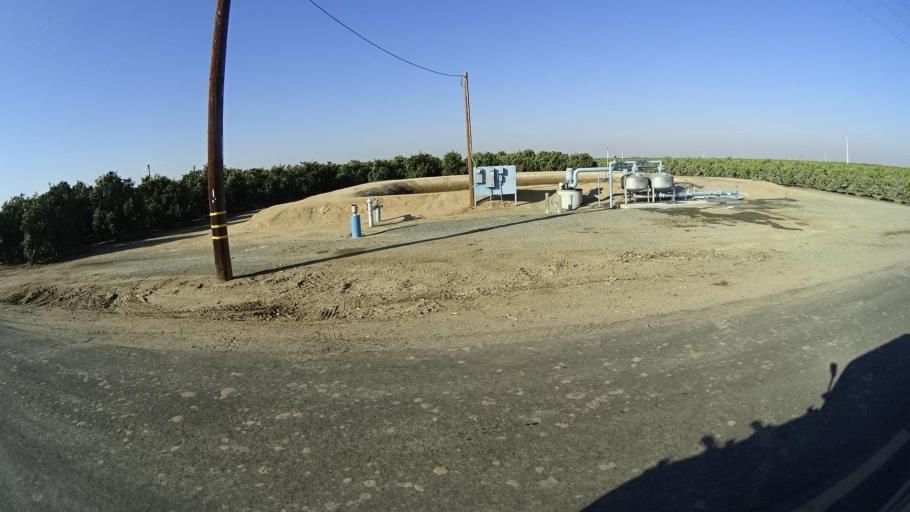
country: US
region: California
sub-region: Tulare County
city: Richgrove
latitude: 35.7285
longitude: -119.1340
